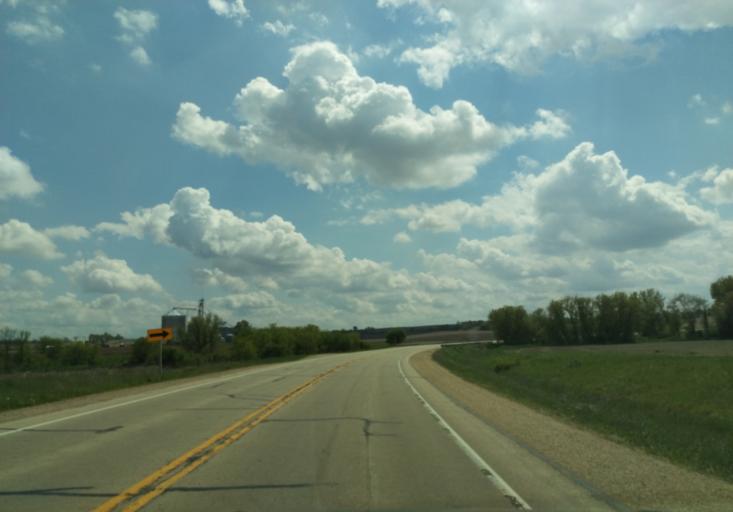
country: US
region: Wisconsin
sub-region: Green County
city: Monticello
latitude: 42.7162
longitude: -89.5983
